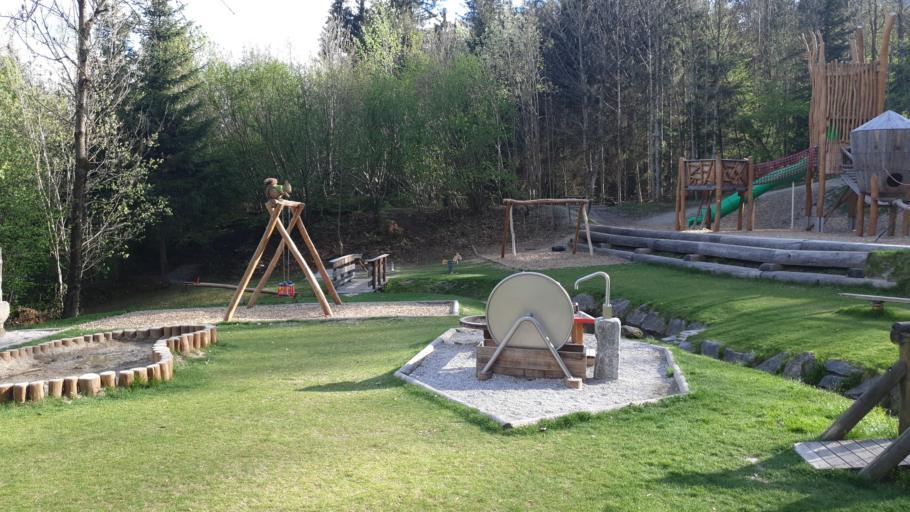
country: AT
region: Tyrol
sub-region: Politischer Bezirk Schwaz
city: Fugenberg
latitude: 47.3459
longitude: 11.8417
